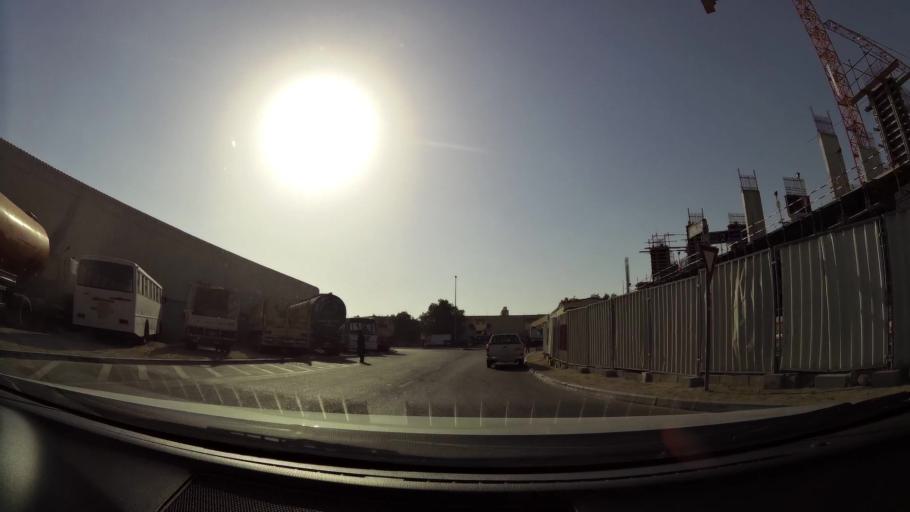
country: AE
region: Dubai
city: Dubai
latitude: 25.1252
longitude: 55.2297
